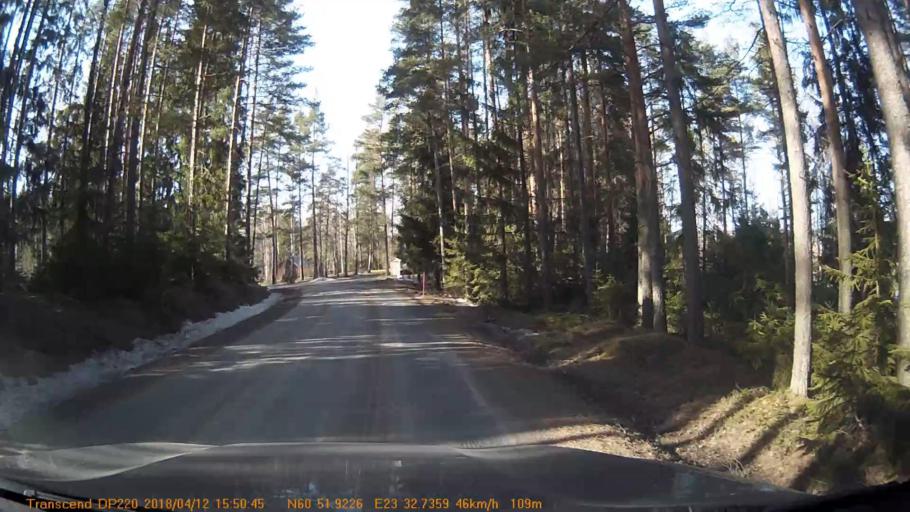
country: FI
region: Haeme
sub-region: Forssa
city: Jokioinen
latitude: 60.8655
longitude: 23.5454
